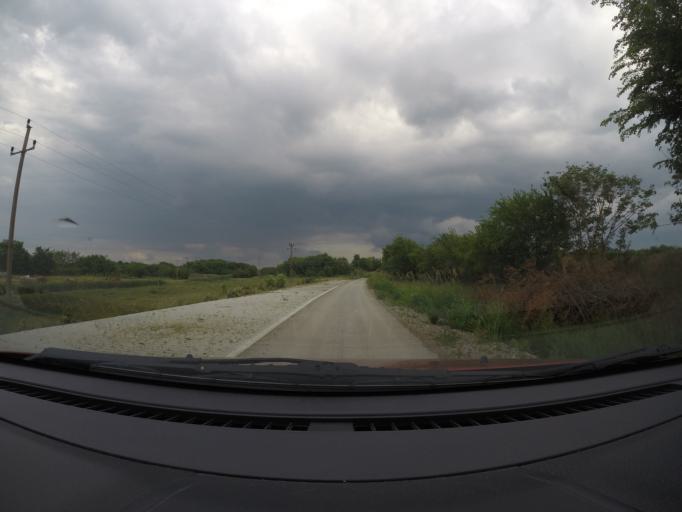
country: RS
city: Uzdin
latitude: 45.2003
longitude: 20.6099
